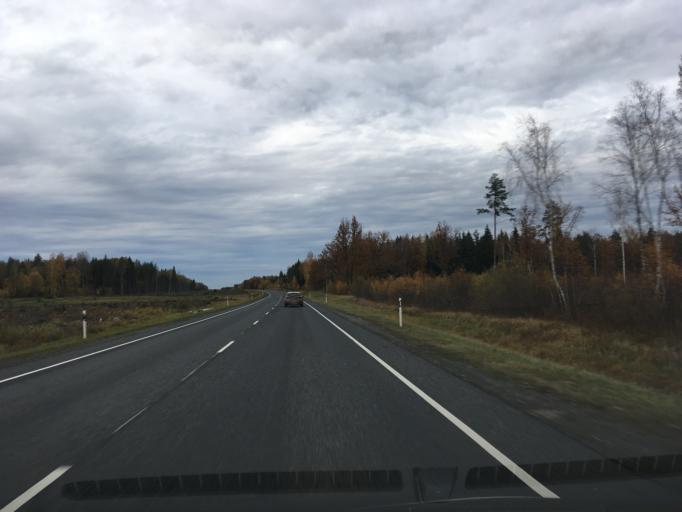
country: EE
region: Harju
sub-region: Nissi vald
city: Turba
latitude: 58.9482
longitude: 24.0839
